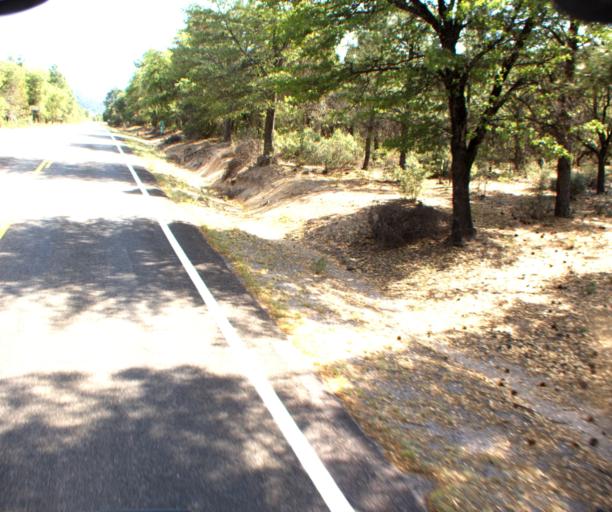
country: US
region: Arizona
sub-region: Greenlee County
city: Clifton
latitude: 33.0612
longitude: -109.0805
